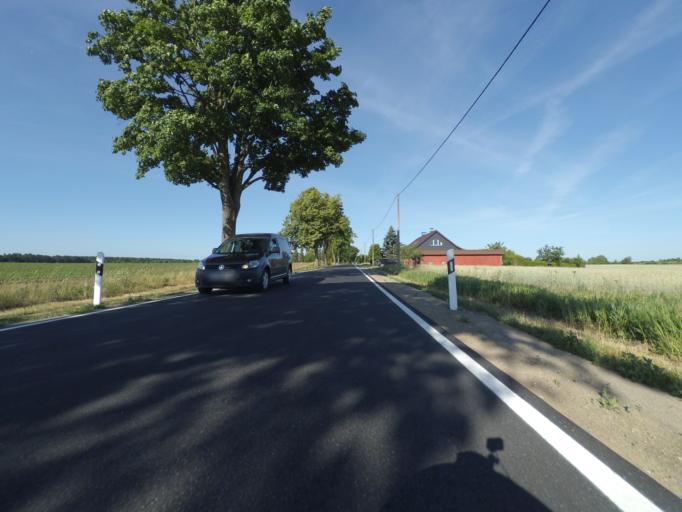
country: DE
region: Mecklenburg-Vorpommern
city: Plau am See
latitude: 53.3699
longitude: 12.2052
